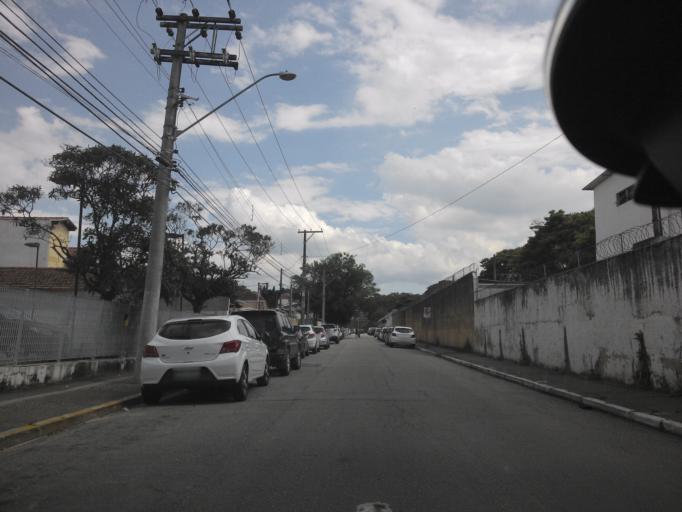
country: BR
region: Sao Paulo
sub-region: Taubate
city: Taubate
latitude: -23.0365
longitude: -45.5730
